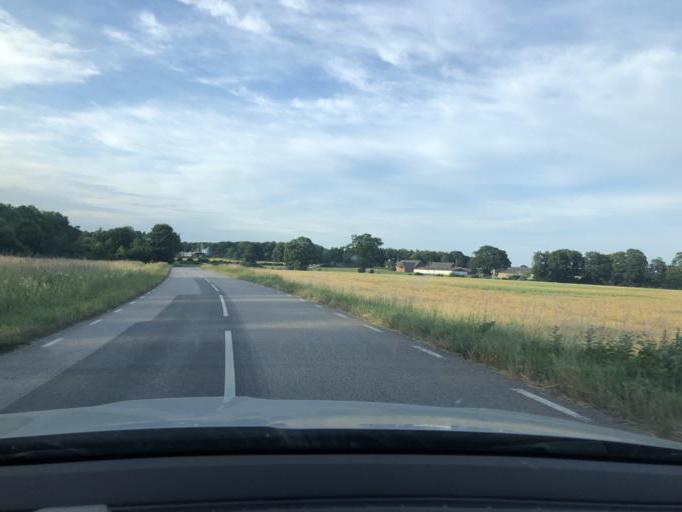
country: SE
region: Blekinge
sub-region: Solvesborgs Kommun
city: Soelvesborg
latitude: 56.0898
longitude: 14.6076
